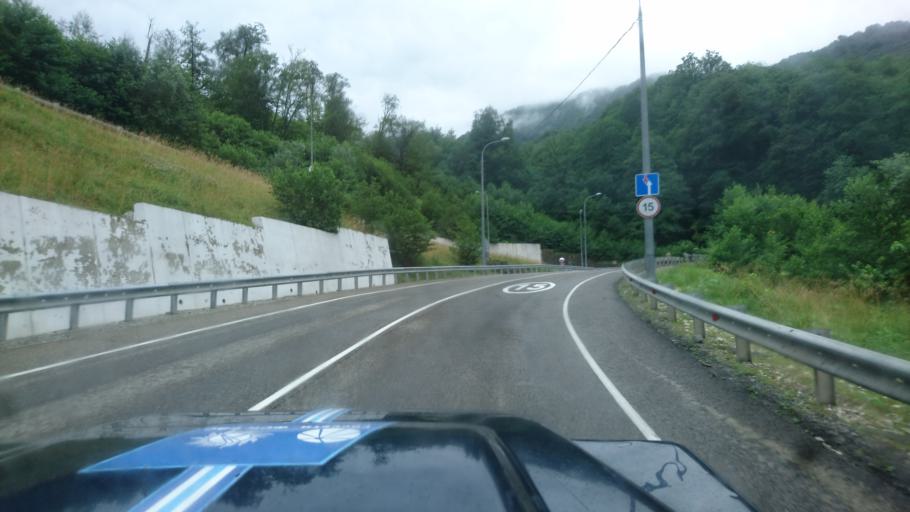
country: RU
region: Krasnodarskiy
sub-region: Sochi City
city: Krasnaya Polyana
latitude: 43.6725
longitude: 40.2860
